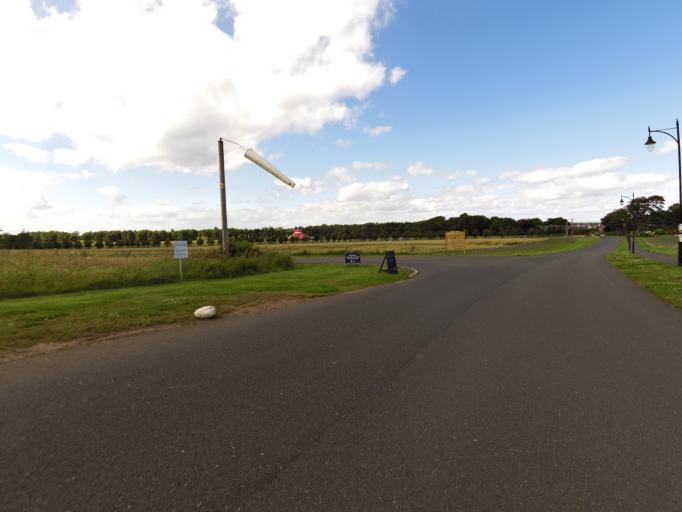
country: GB
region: Scotland
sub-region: East Lothian
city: Gullane
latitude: 56.0445
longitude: -2.7973
